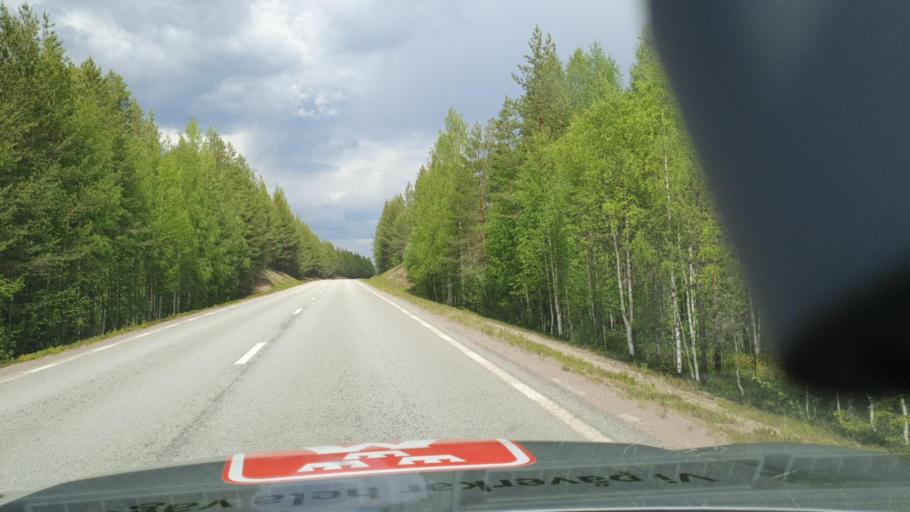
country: SE
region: Vaesterbotten
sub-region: Asele Kommun
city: Asele
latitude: 63.8812
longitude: 17.2063
